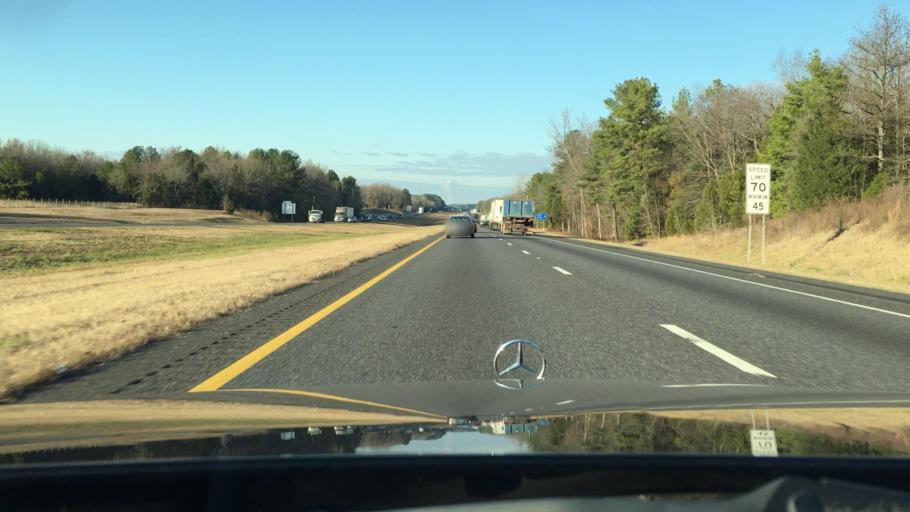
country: US
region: South Carolina
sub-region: York County
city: Lesslie
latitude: 34.7574
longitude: -81.0363
